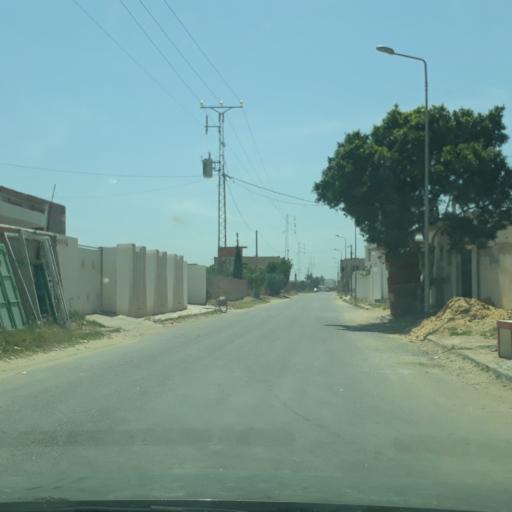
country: TN
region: Safaqis
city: Al Qarmadah
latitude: 34.8266
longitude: 10.7836
